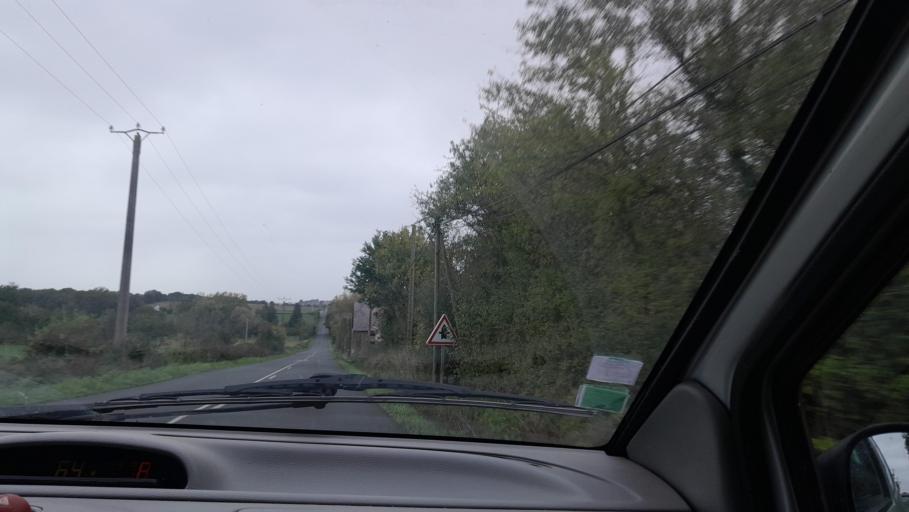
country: FR
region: Pays de la Loire
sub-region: Departement de Maine-et-Loire
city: Pouance
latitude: 47.7187
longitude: -1.1778
